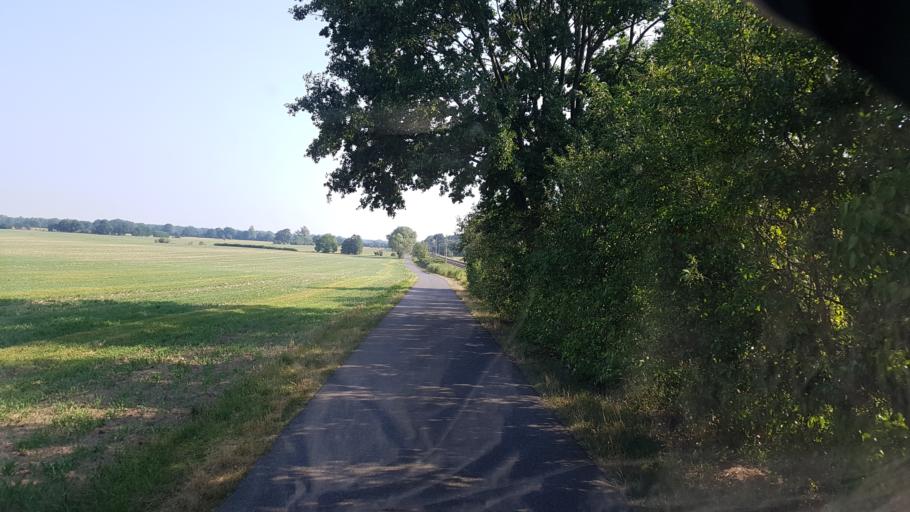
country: DE
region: Brandenburg
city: Drebkau
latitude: 51.6706
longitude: 14.2419
